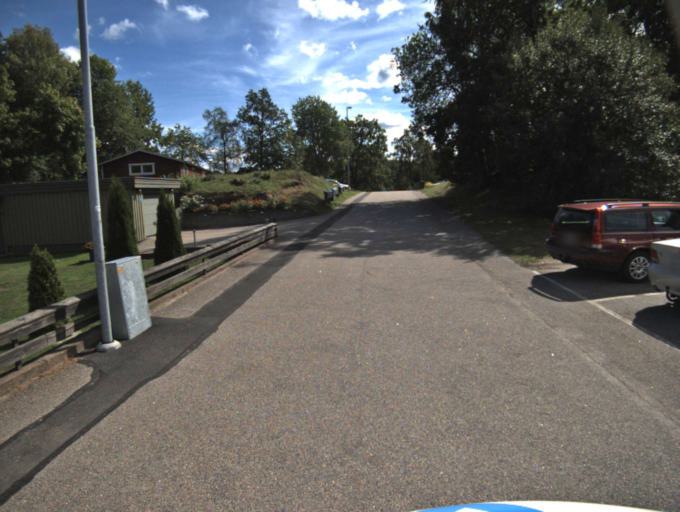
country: SE
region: Vaestra Goetaland
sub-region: Ulricehamns Kommun
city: Ulricehamn
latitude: 57.9029
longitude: 13.4718
